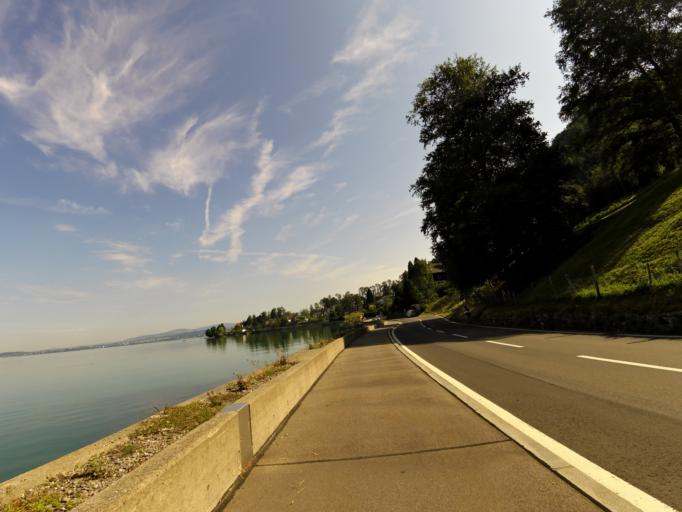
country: CH
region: Zug
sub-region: Zug
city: Walchwil
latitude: 47.1339
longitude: 8.5046
